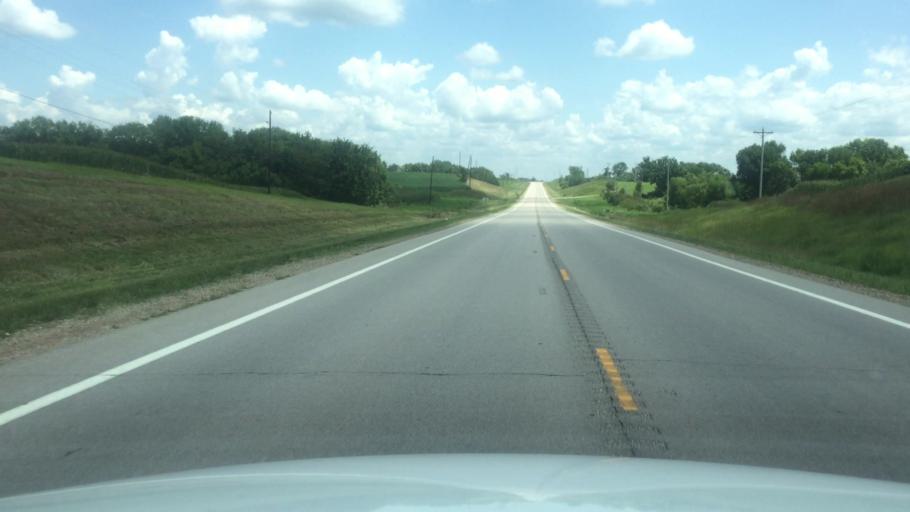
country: US
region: Kansas
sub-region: Brown County
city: Horton
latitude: 39.6675
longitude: -95.5015
